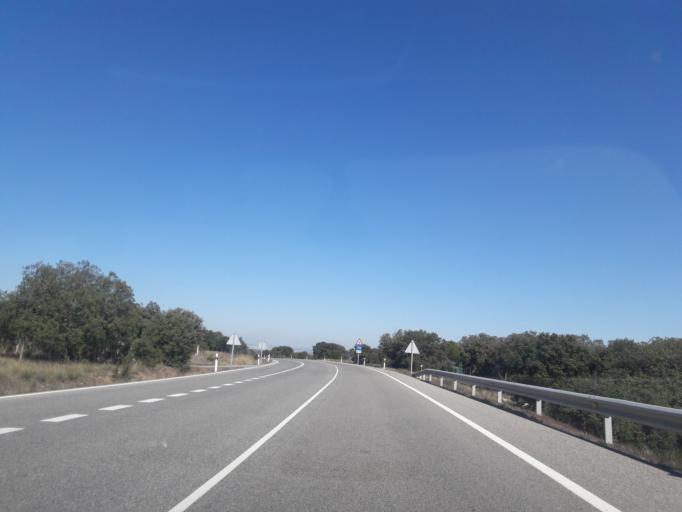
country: ES
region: Castille and Leon
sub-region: Provincia de Salamanca
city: Martinamor
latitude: 40.8135
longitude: -5.6286
